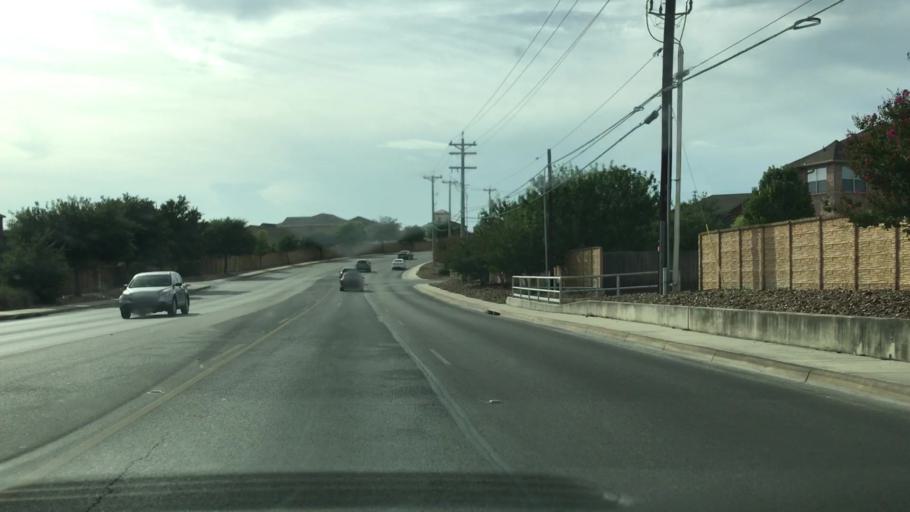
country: US
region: Texas
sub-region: Guadalupe County
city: Northcliff
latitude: 29.5978
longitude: -98.2577
